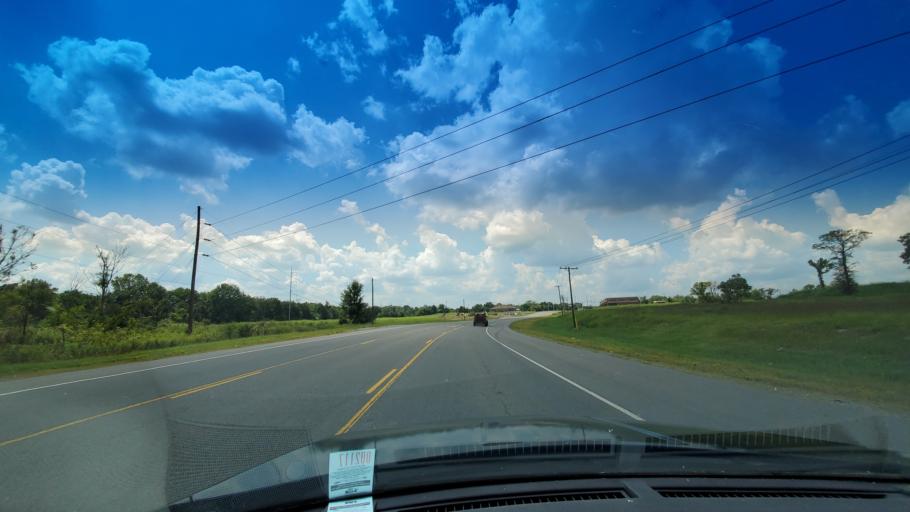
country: US
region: Tennessee
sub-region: Wilson County
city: Lebanon
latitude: 36.1738
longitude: -86.3044
